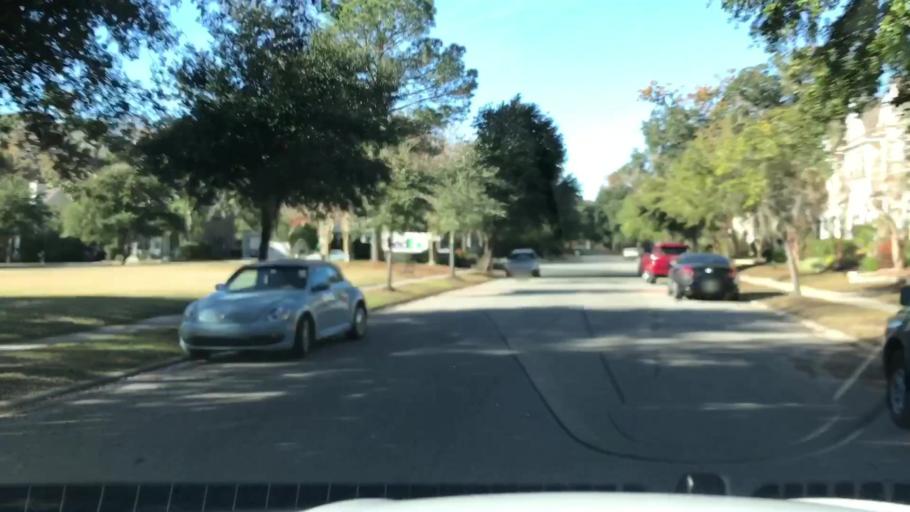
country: US
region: South Carolina
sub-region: Beaufort County
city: Bluffton
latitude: 32.2691
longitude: -80.8708
